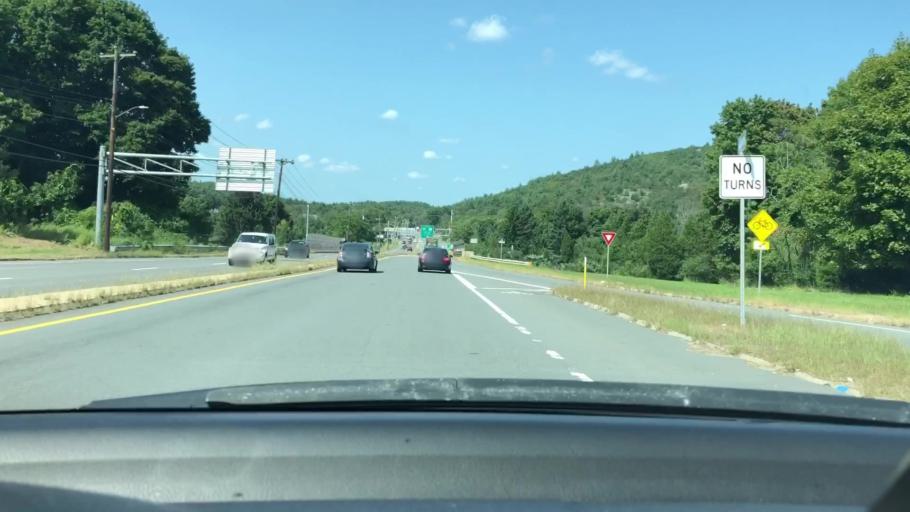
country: US
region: Massachusetts
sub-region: Norfolk County
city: Canton
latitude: 42.2019
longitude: -71.1190
